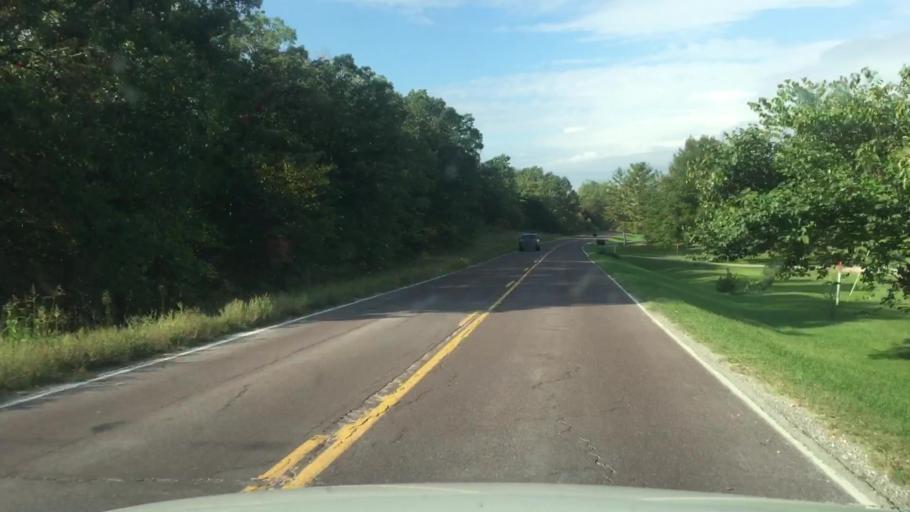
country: US
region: Missouri
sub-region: Boone County
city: Columbia
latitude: 38.8655
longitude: -92.3059
